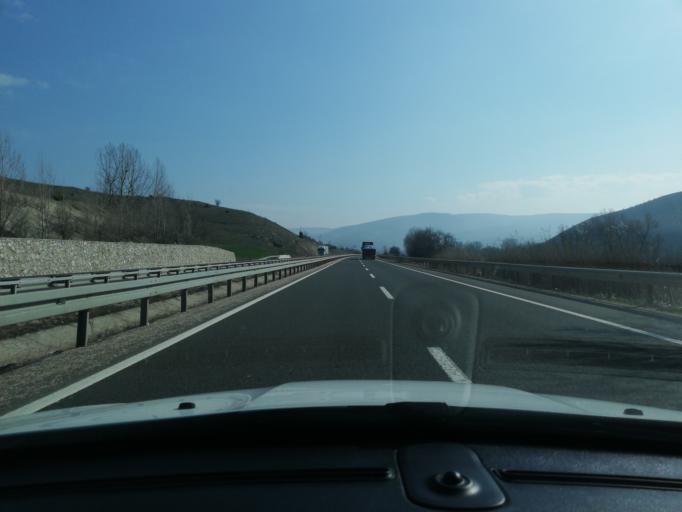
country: TR
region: Cankiri
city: Cerkes
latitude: 40.8343
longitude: 32.7400
